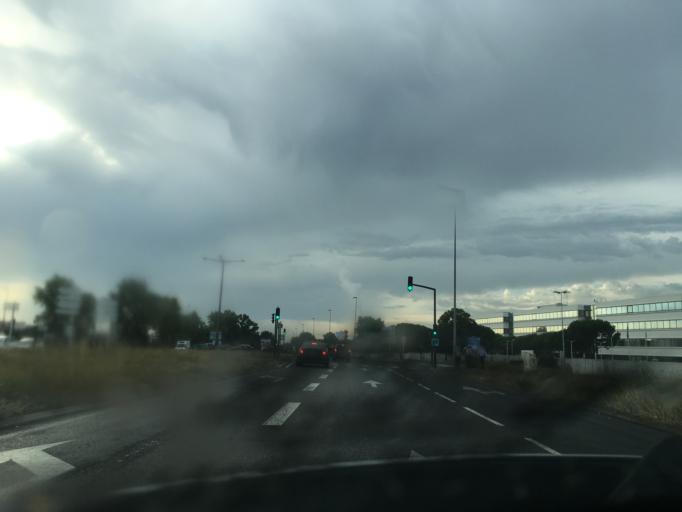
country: FR
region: Midi-Pyrenees
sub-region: Departement de la Haute-Garonne
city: Portet-sur-Garonne
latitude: 43.5622
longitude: 1.3896
